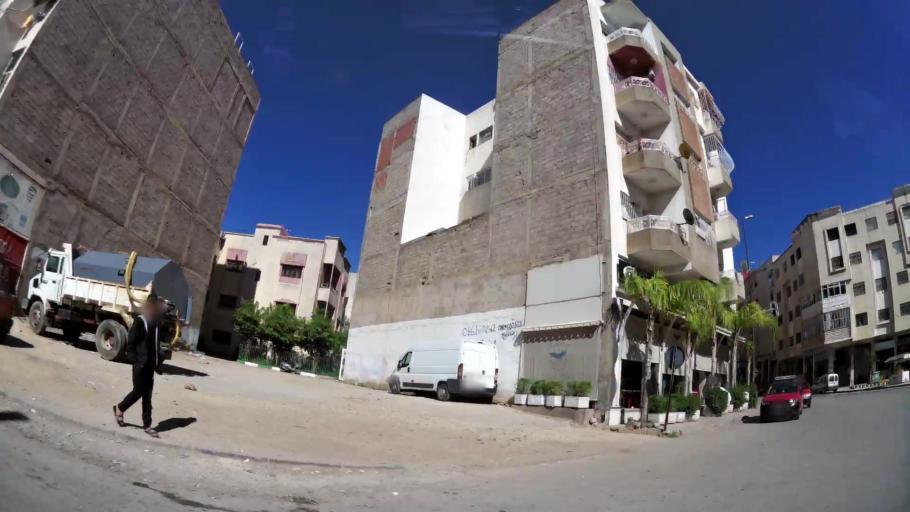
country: MA
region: Fes-Boulemane
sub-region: Fes
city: Fes
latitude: 34.0183
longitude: -4.9814
